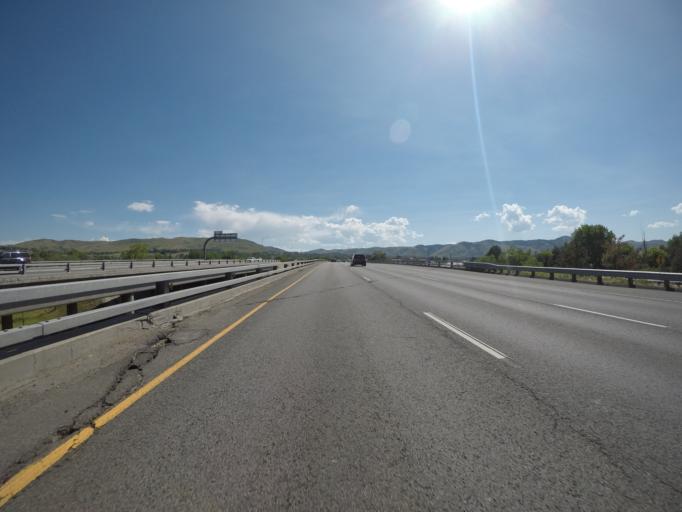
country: US
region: Colorado
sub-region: Jefferson County
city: West Pleasant View
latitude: 39.7313
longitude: -105.1704
